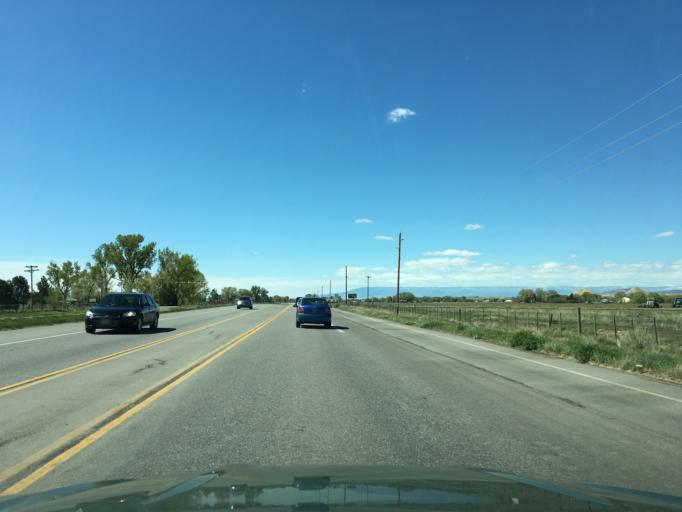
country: US
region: Colorado
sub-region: Montrose County
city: Montrose
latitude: 38.3913
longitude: -107.8301
